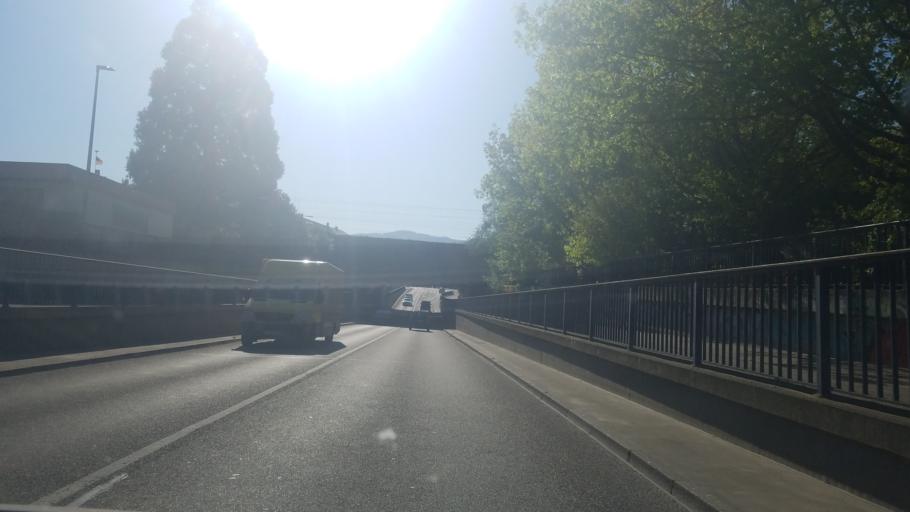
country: DE
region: Baden-Wuerttemberg
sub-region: Karlsruhe Region
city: Buhl
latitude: 48.7002
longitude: 8.1304
